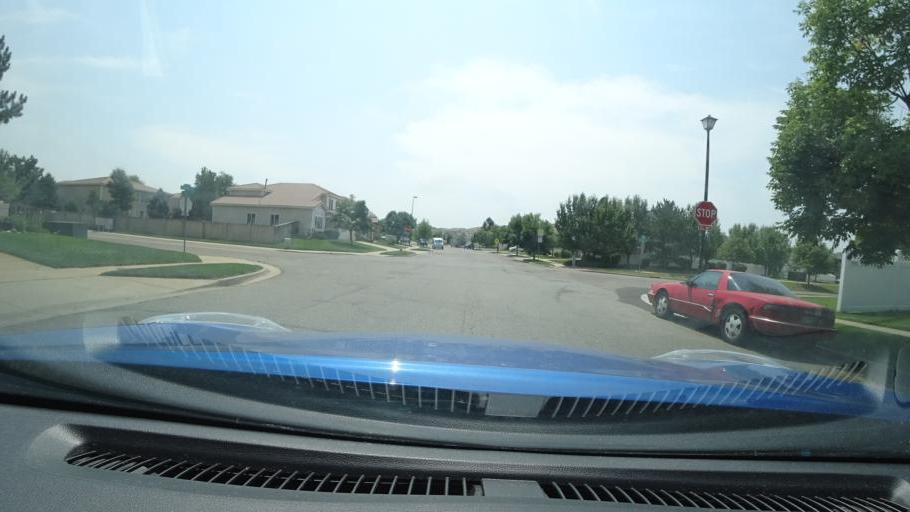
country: US
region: Colorado
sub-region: Adams County
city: Aurora
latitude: 39.7749
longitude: -104.7691
